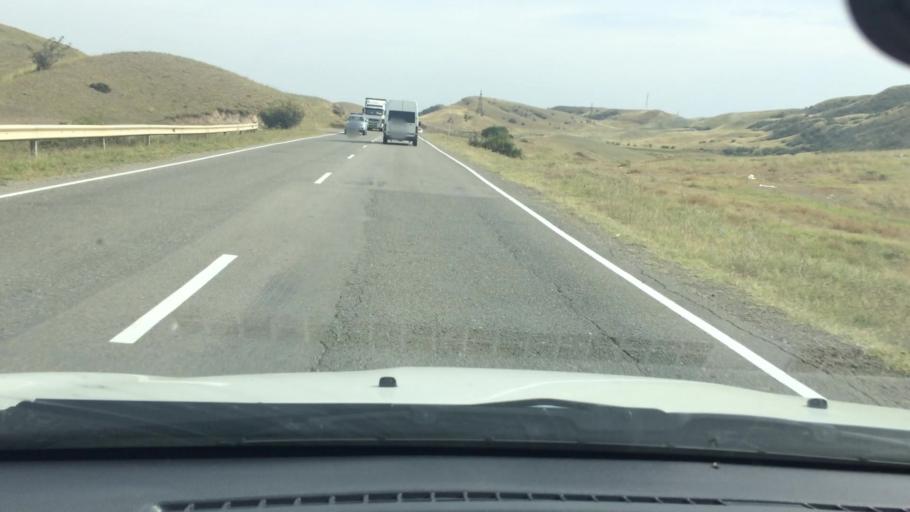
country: GE
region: Kvemo Kartli
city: Rust'avi
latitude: 41.5328
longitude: 44.9827
